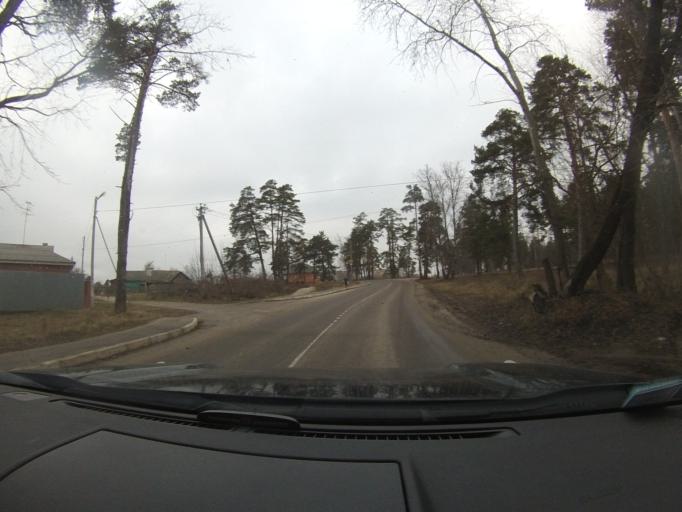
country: RU
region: Moskovskaya
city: Peski
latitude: 55.2648
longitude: 38.7588
